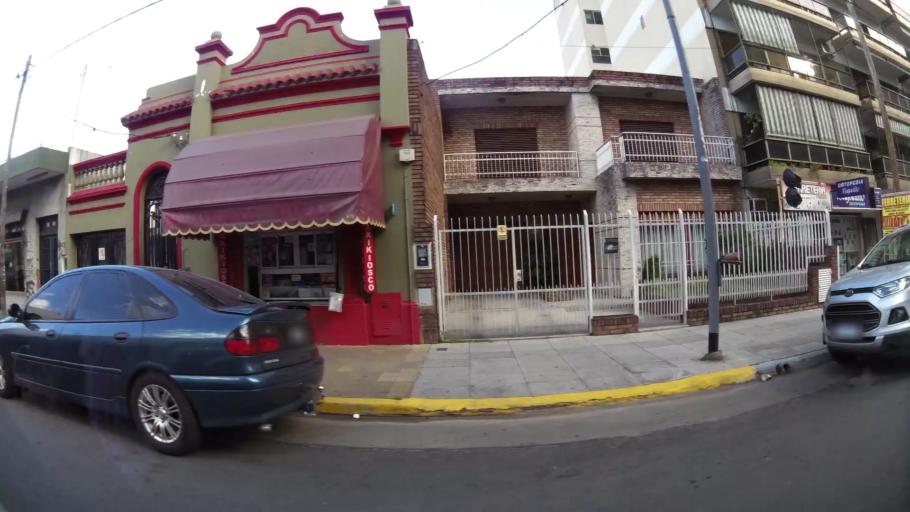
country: AR
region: Buenos Aires
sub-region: Partido de General San Martin
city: General San Martin
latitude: -34.5470
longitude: -58.5509
